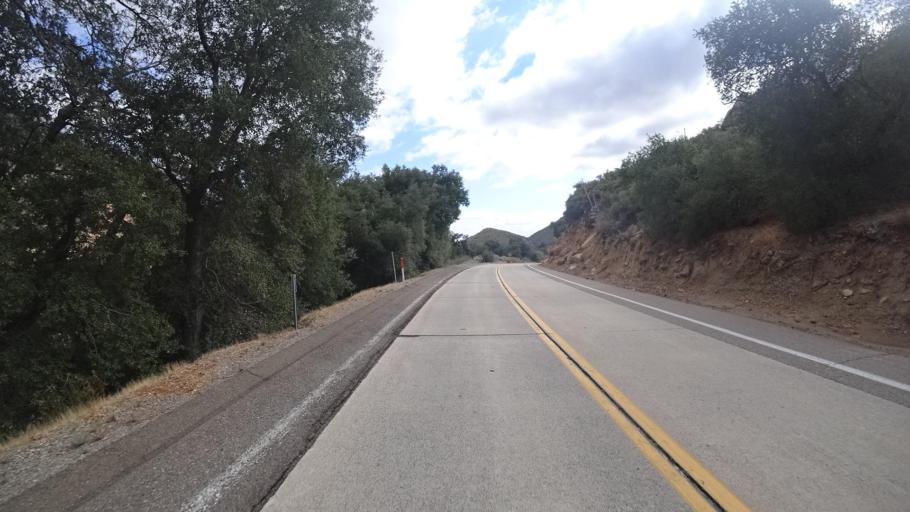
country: US
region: California
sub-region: San Diego County
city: Pine Valley
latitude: 32.7924
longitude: -116.4967
